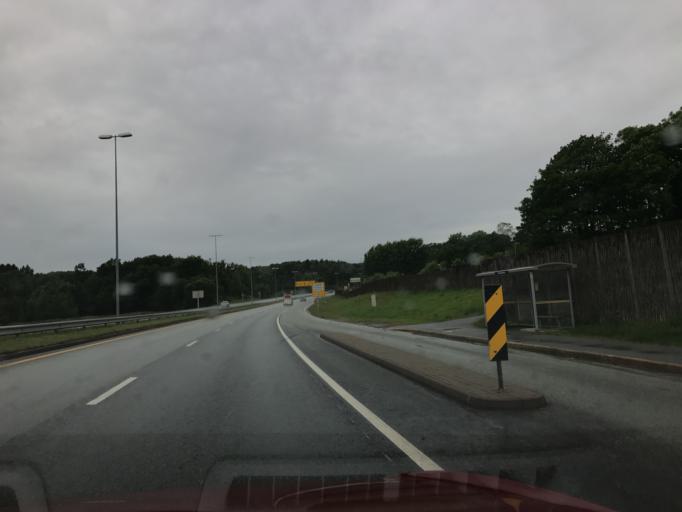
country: NO
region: Vest-Agder
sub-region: Kristiansand
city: Tveit
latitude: 58.1679
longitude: 8.1032
